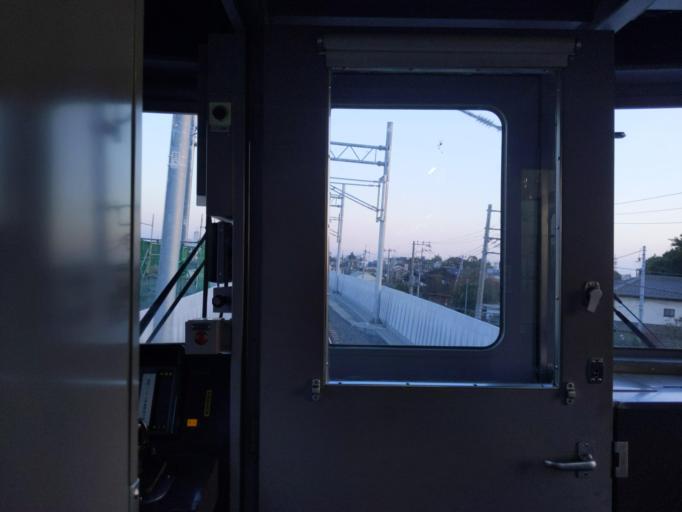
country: JP
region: Chiba
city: Noda
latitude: 35.9520
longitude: 139.8632
